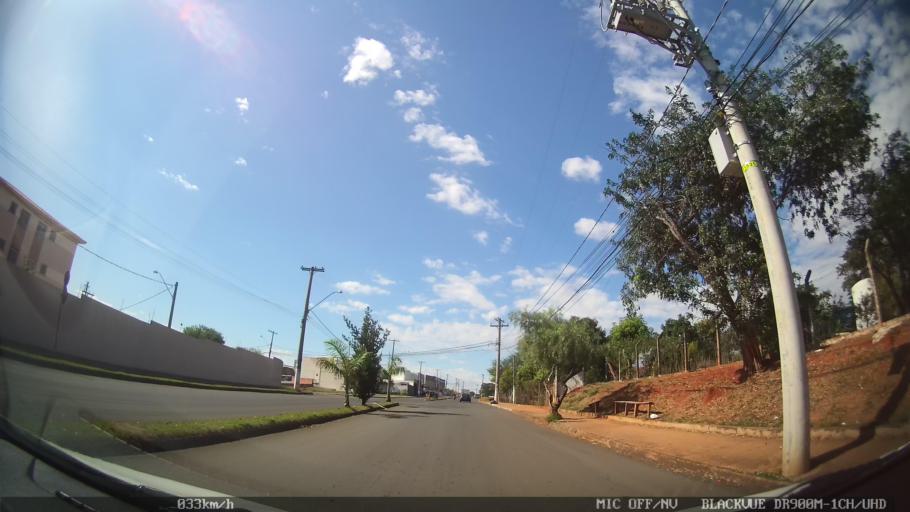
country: BR
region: Sao Paulo
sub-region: Santa Barbara D'Oeste
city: Santa Barbara d'Oeste
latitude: -22.7313
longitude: -47.3920
